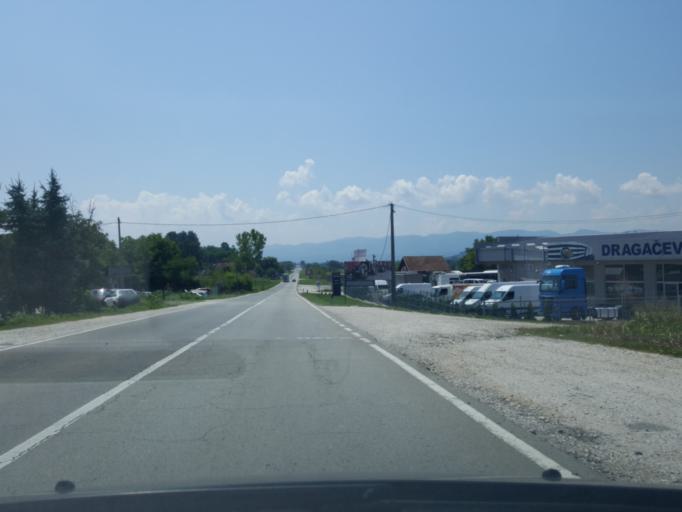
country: RS
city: Prislonica
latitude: 43.9495
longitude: 20.4149
